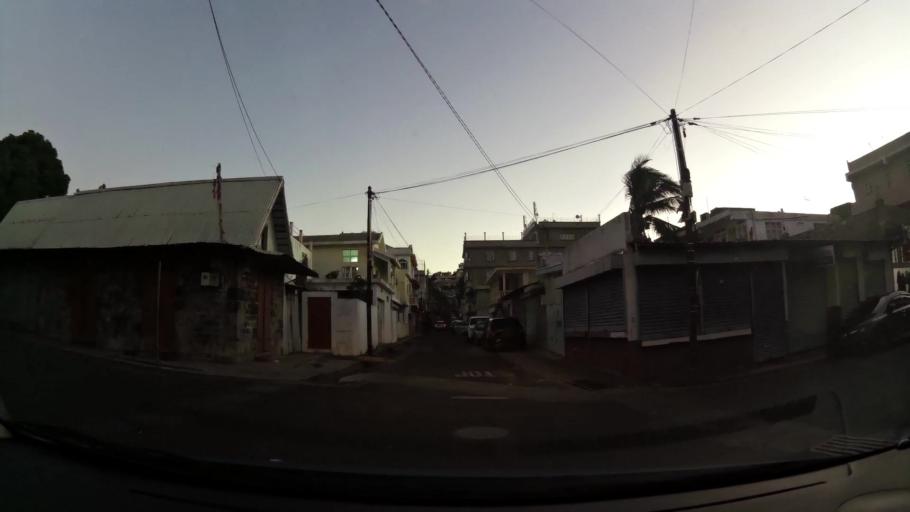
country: MU
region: Port Louis
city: Port Louis
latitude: -20.1656
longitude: 57.5154
